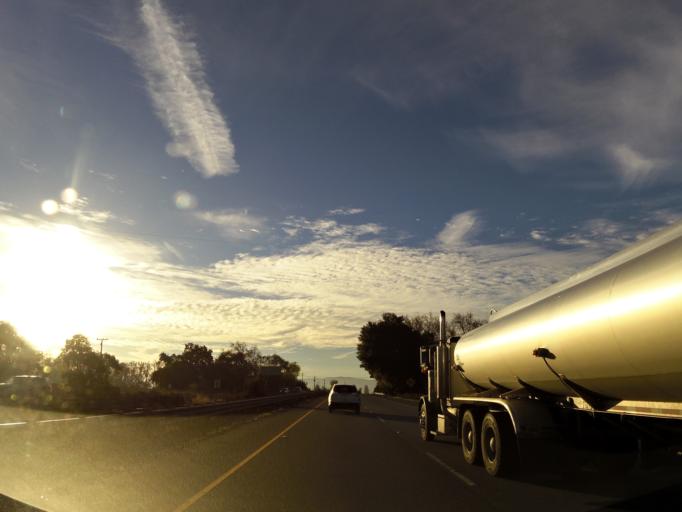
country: US
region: California
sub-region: Santa Clara County
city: Gilroy
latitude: 36.9779
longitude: -121.5564
